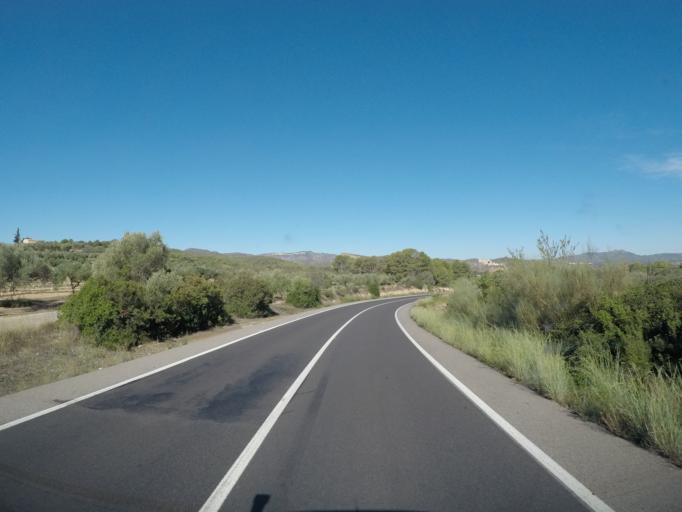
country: ES
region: Catalonia
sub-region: Provincia de Tarragona
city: Rasquera
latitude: 41.0173
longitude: 0.6095
